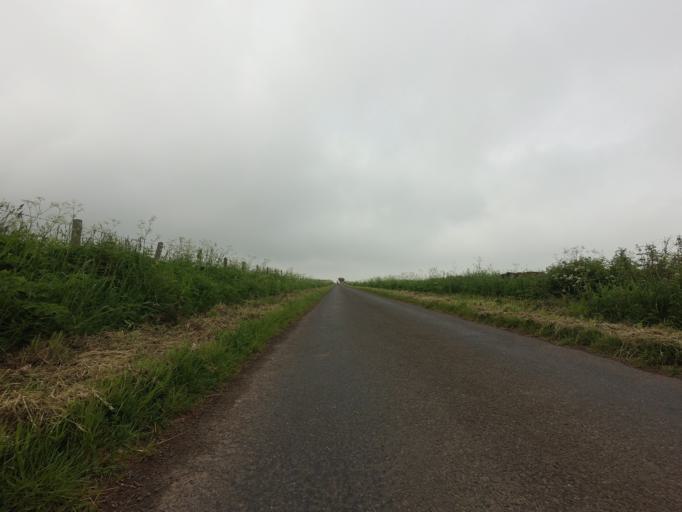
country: GB
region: Scotland
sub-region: Perth and Kinross
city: Milnathort
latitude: 56.2436
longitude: -3.3418
